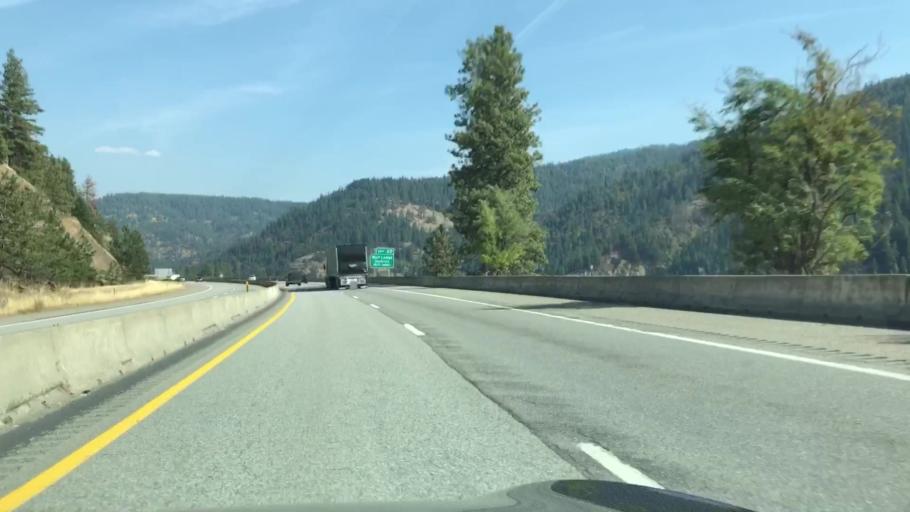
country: US
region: Idaho
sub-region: Kootenai County
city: Coeur d'Alene
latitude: 47.6238
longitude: -116.6647
